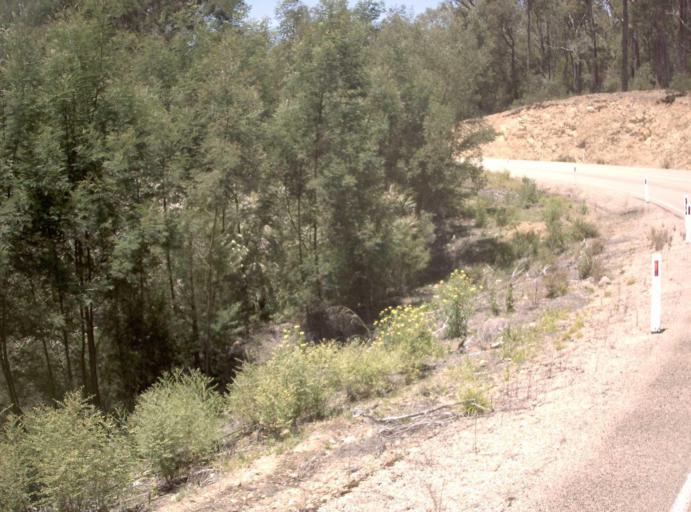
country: AU
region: Victoria
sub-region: East Gippsland
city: Lakes Entrance
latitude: -37.5641
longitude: 147.8875
